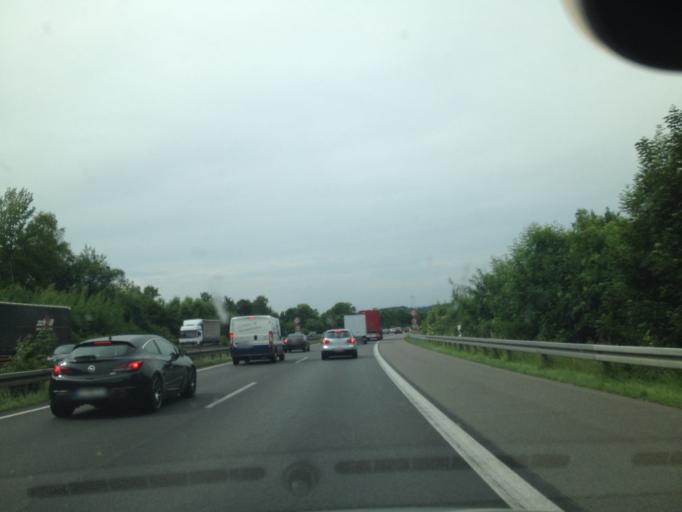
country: DE
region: North Rhine-Westphalia
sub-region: Regierungsbezirk Arnsberg
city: Schalksmuhle
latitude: 51.2933
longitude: 7.5552
